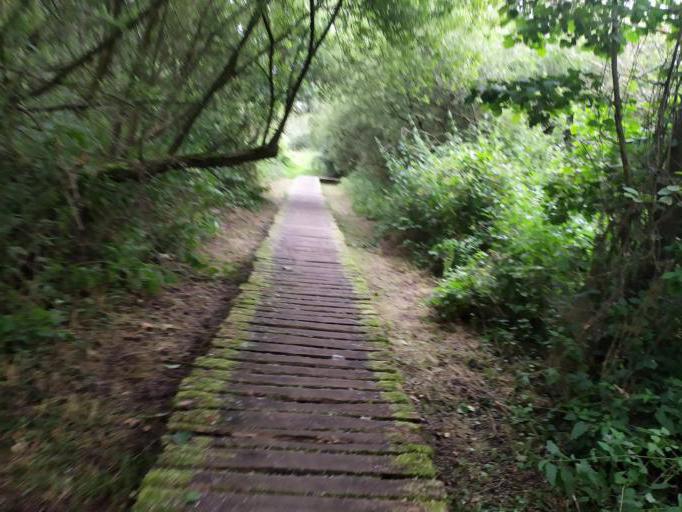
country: BE
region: Flanders
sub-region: Provincie Vlaams-Brabant
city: Oud-Heverlee
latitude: 50.7934
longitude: 4.6403
